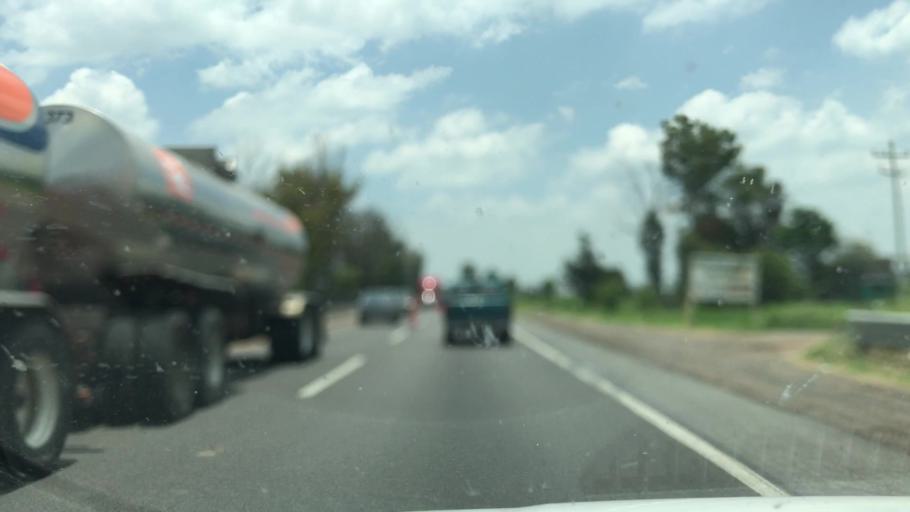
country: MX
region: Guanajuato
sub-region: Abasolo
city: San Bernardo Pena Blanca
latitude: 20.5037
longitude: -101.4766
